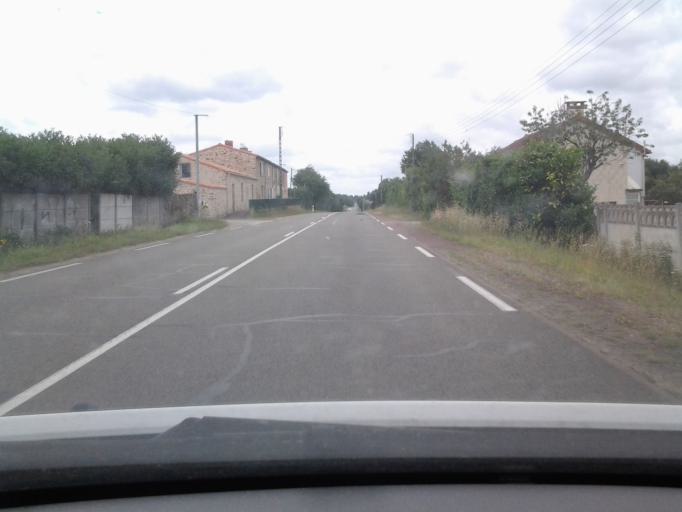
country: FR
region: Pays de la Loire
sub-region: Departement de la Vendee
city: Les Clouzeaux
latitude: 46.6563
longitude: -1.4846
